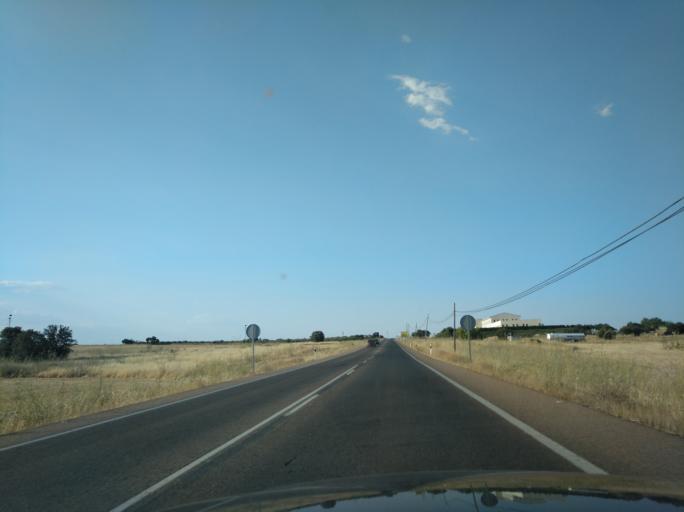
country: ES
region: Extremadura
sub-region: Provincia de Badajoz
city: Olivenza
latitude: 38.7059
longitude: -7.0868
